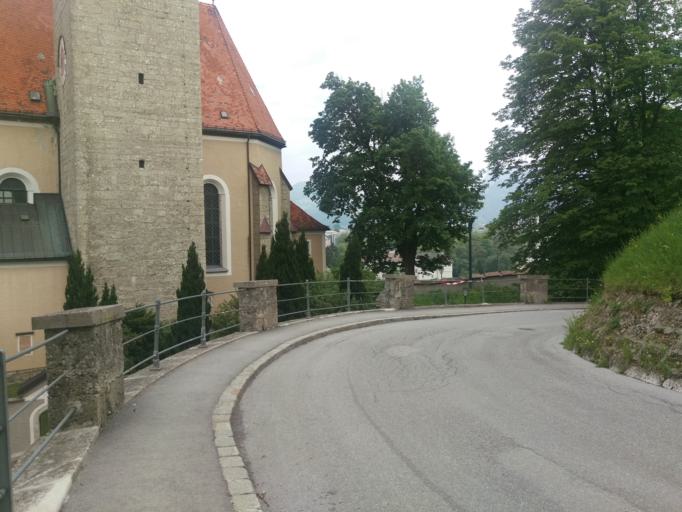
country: AT
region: Salzburg
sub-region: Salzburg Stadt
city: Salzburg
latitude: 47.8052
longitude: 13.0348
